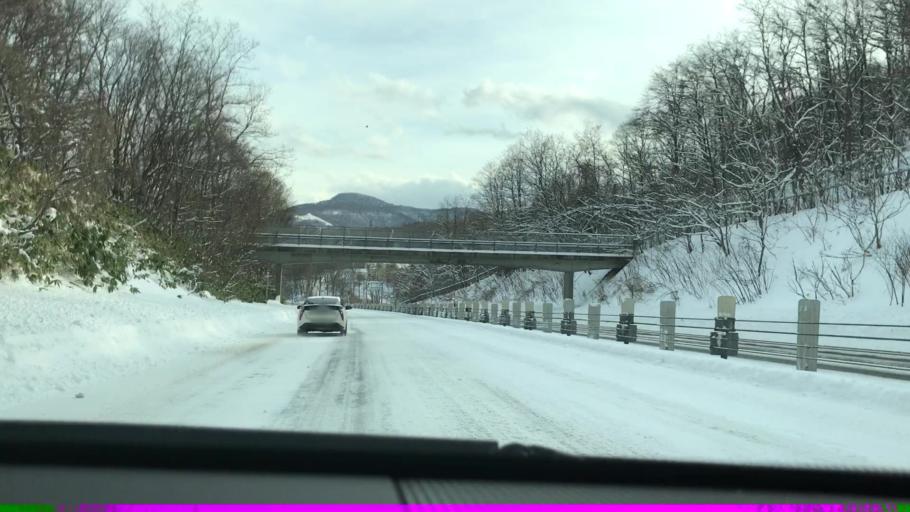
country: JP
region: Hokkaido
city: Otaru
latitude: 43.1492
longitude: 141.1299
